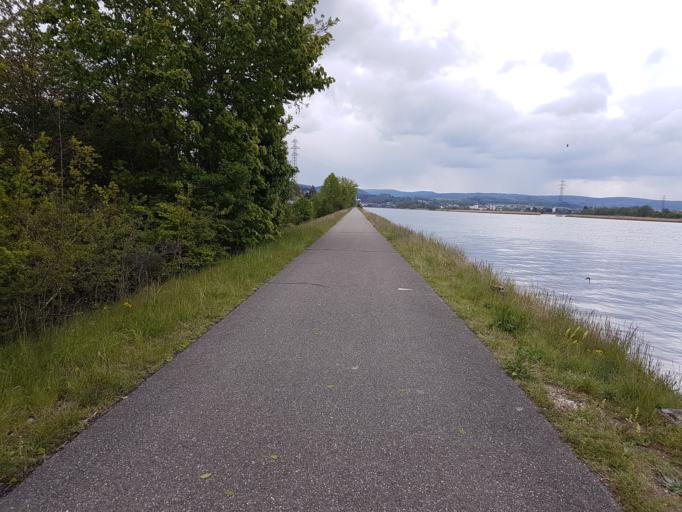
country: CH
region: Aargau
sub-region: Bezirk Zurzach
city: Klingnau
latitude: 47.5887
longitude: 8.2330
